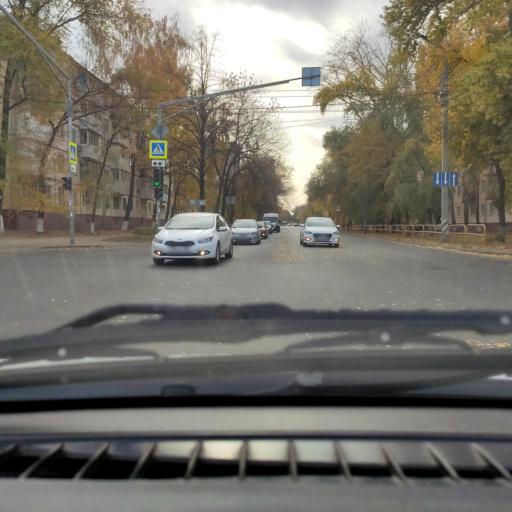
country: RU
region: Samara
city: Tol'yatti
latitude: 53.5180
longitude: 49.4254
